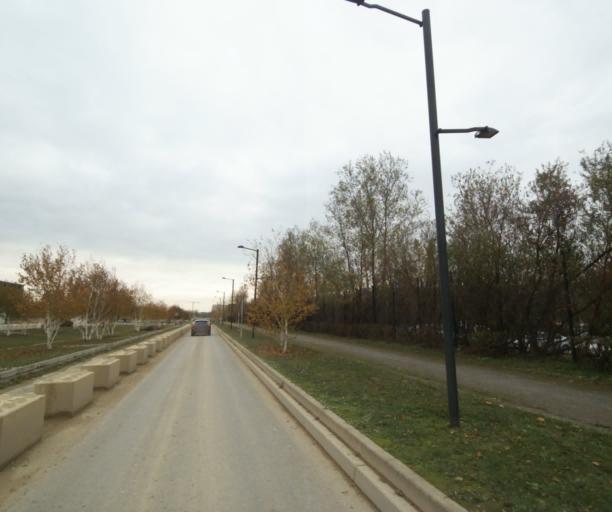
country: FR
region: Ile-de-France
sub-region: Departement du Val-d'Oise
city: Gonesse
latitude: 48.9692
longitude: 2.4606
